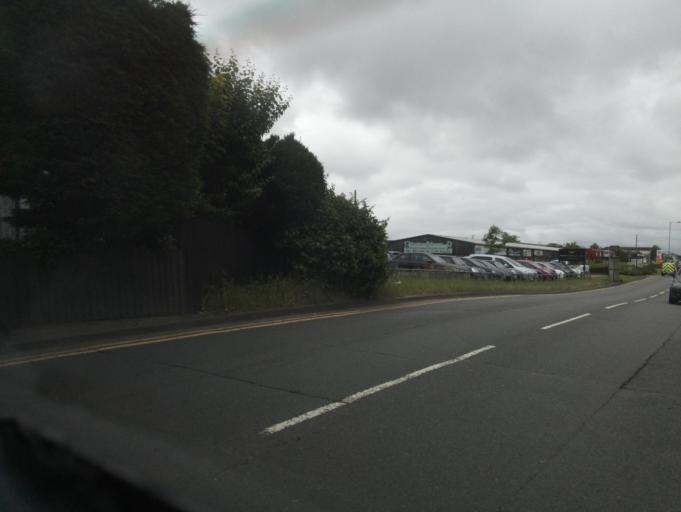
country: GB
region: England
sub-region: Staffordshire
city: Burton upon Trent
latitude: 52.8192
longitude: -1.6285
